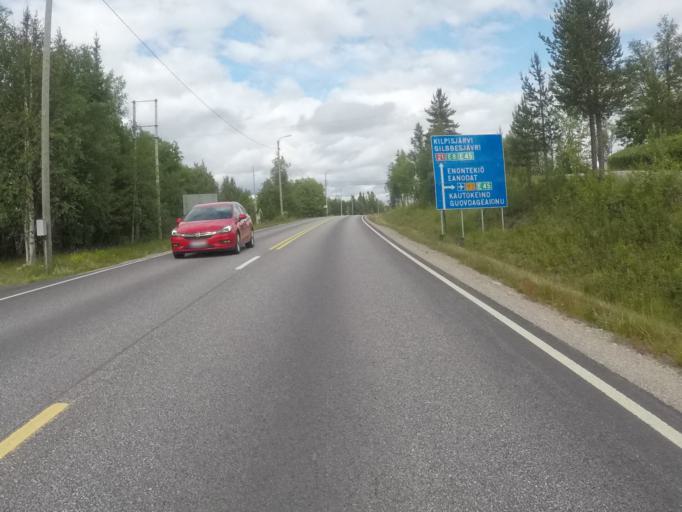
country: FI
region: Lapland
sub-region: Tunturi-Lappi
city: Enontekioe
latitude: 68.2817
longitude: 23.0821
